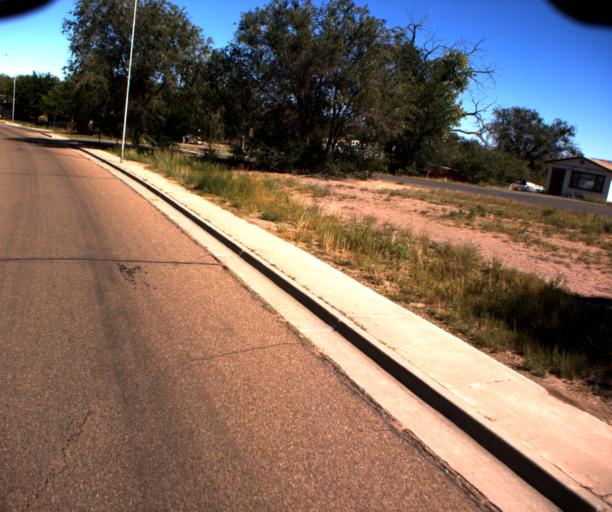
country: US
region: Arizona
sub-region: Apache County
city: Saint Johns
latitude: 34.5021
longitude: -109.3616
